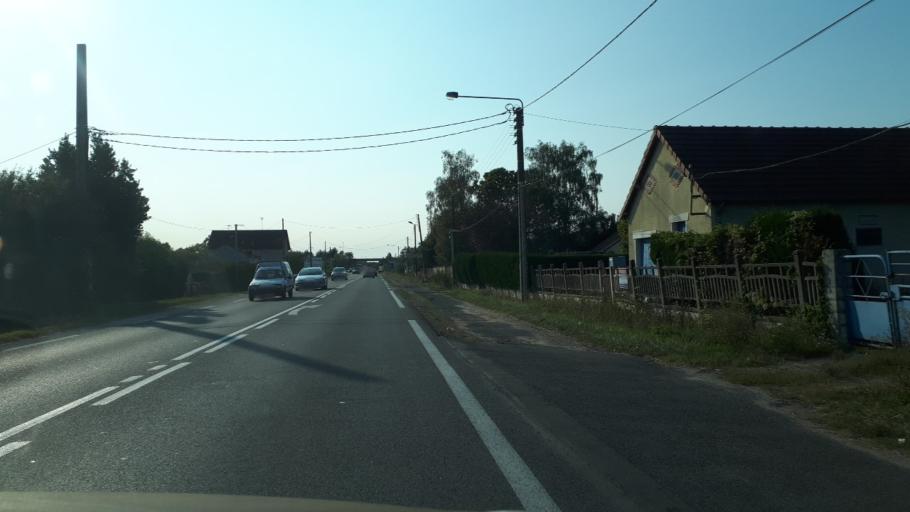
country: FR
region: Centre
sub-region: Departement du Cher
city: Vierzon
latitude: 47.2141
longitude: 2.1229
